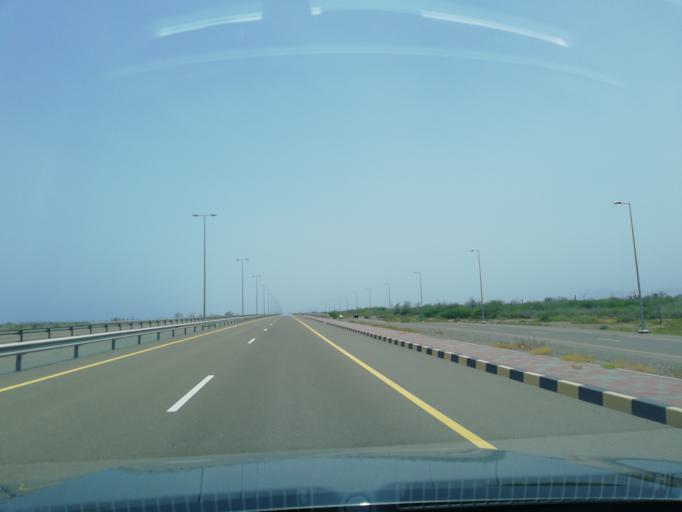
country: OM
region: Al Batinah
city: Shinas
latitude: 24.8881
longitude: 56.4018
